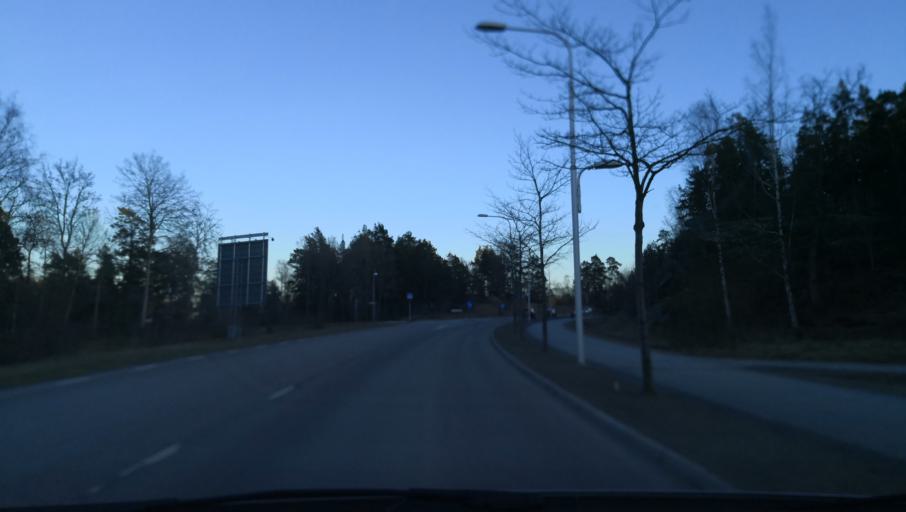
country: SE
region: Stockholm
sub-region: Varmdo Kommun
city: Gustavsberg
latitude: 59.3171
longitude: 18.3905
